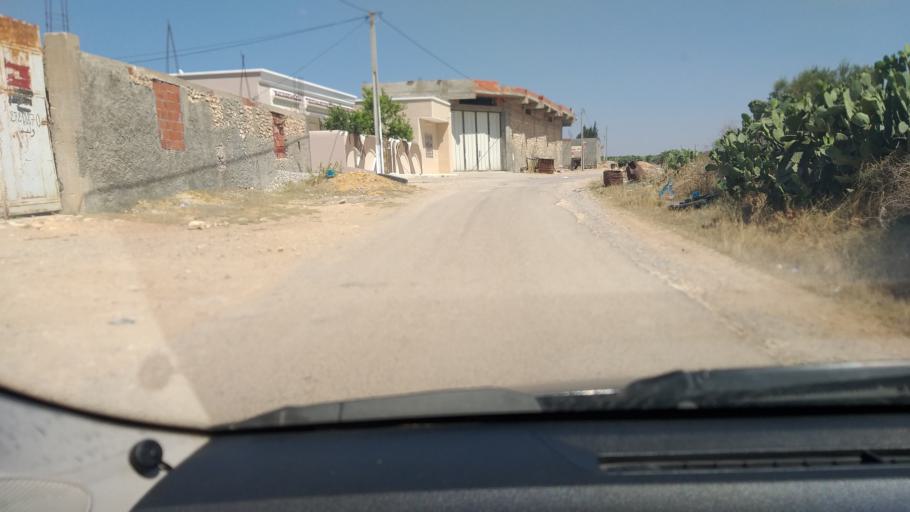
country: TN
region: Al Mahdiyah
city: El Jem
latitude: 35.2887
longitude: 10.7217
